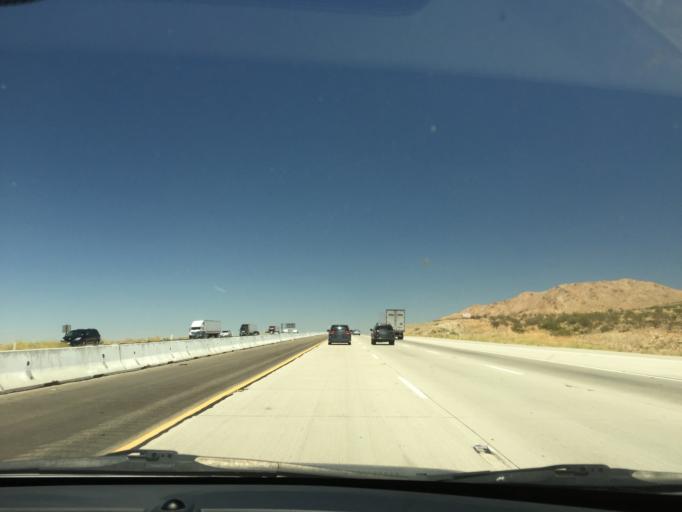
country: US
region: California
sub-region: San Bernardino County
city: Victorville
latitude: 34.7033
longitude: -117.2044
